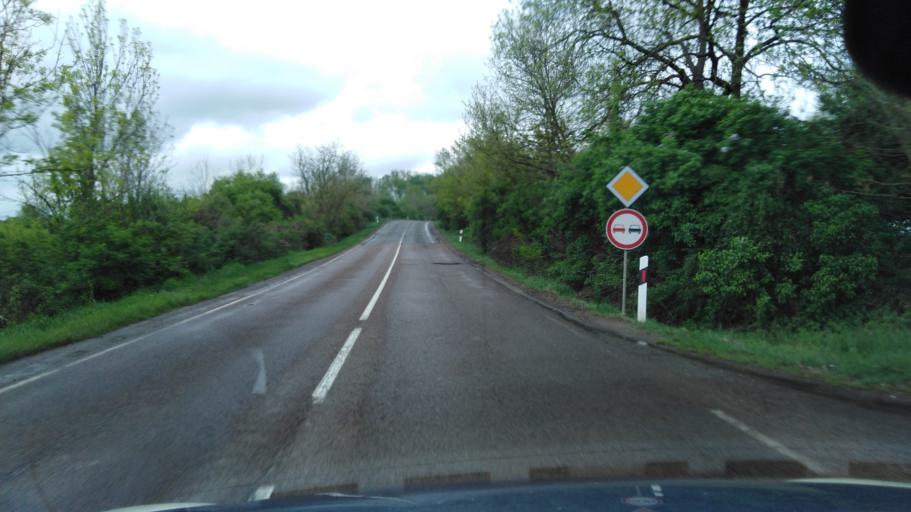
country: HU
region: Nograd
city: Szecseny
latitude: 48.0924
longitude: 19.5315
